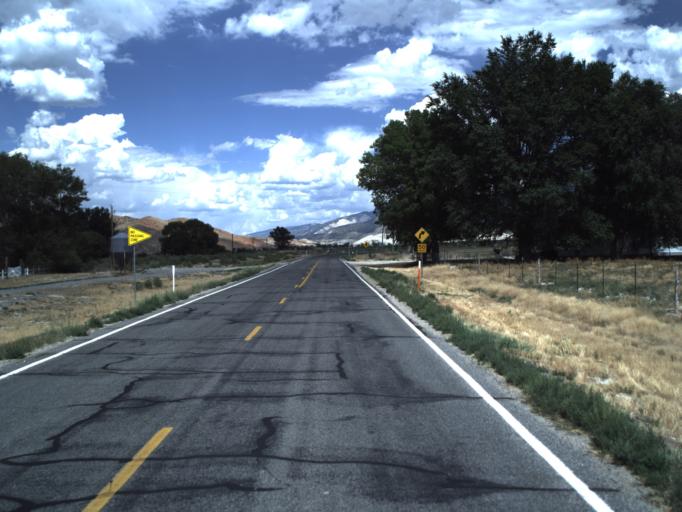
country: US
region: Utah
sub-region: Sanpete County
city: Gunnison
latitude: 39.1421
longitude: -111.7663
